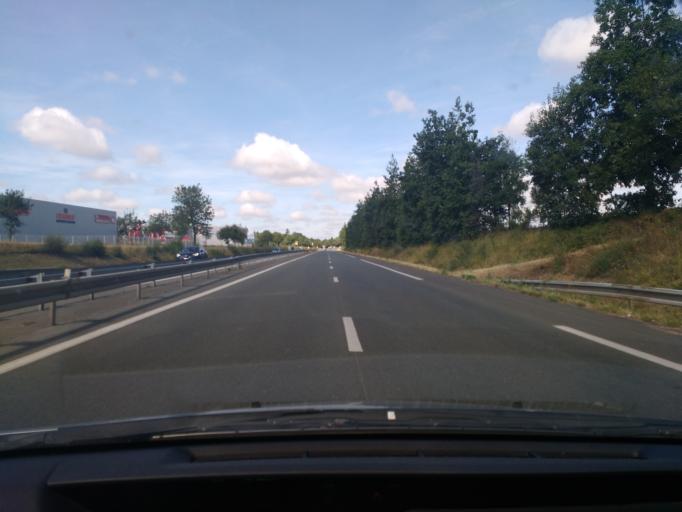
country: FR
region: Pays de la Loire
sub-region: Departement de Maine-et-Loire
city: Saint-Lambert-la-Potherie
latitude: 47.4655
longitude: -0.6648
